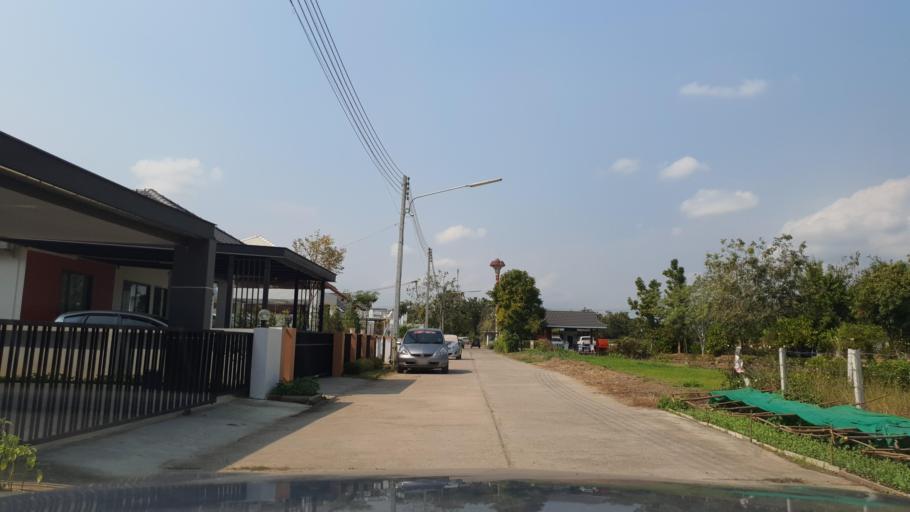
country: TH
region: Chiang Mai
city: San Pa Tong
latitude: 18.6537
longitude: 98.8926
